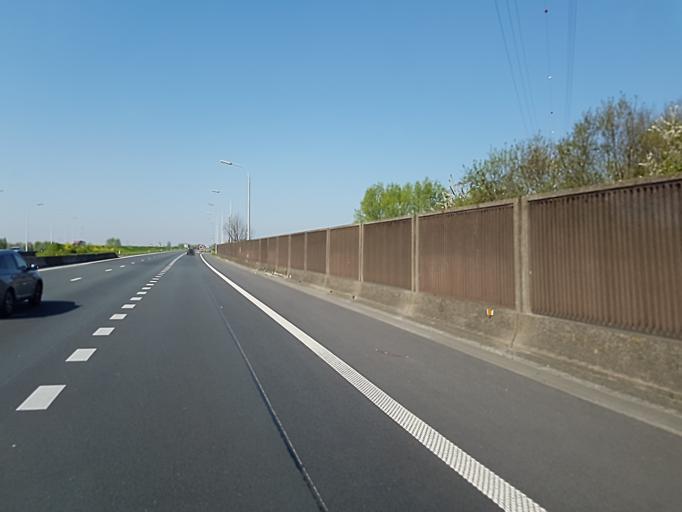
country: BE
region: Flanders
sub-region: Provincie West-Vlaanderen
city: Menen
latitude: 50.8178
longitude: 3.1347
